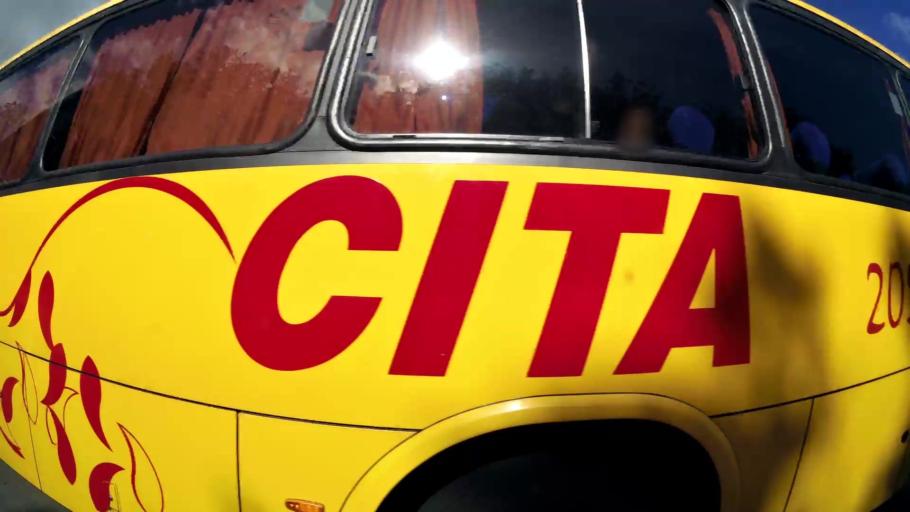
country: UY
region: Montevideo
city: Montevideo
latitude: -34.8395
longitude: -56.2216
